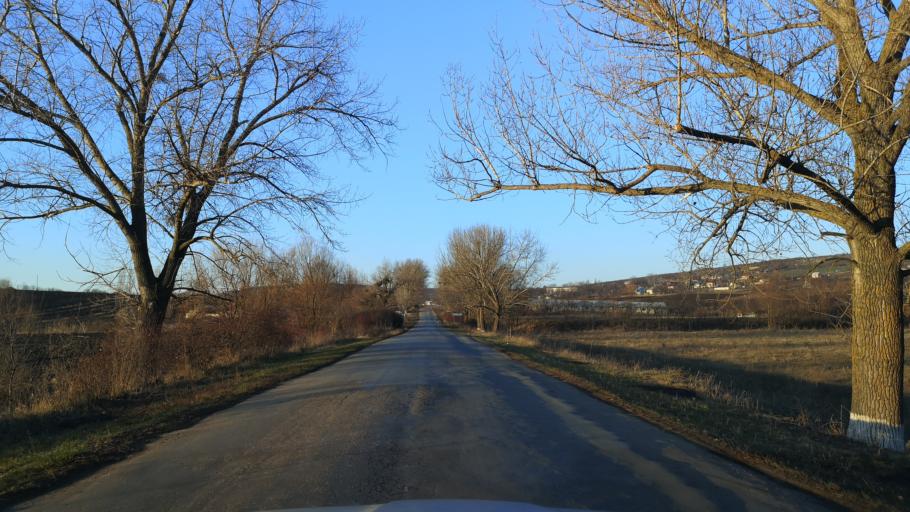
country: MD
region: Orhei
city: Orhei
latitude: 47.3455
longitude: 28.6979
